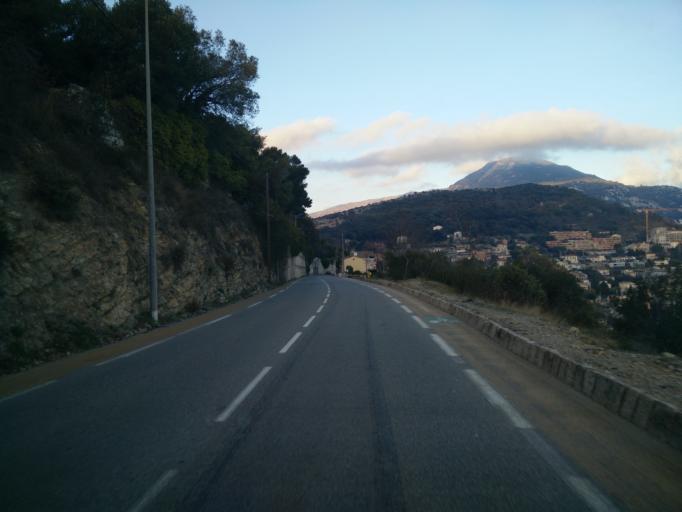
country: FR
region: Provence-Alpes-Cote d'Azur
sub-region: Departement des Alpes-Maritimes
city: La Turbie
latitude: 43.7405
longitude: 7.3905
